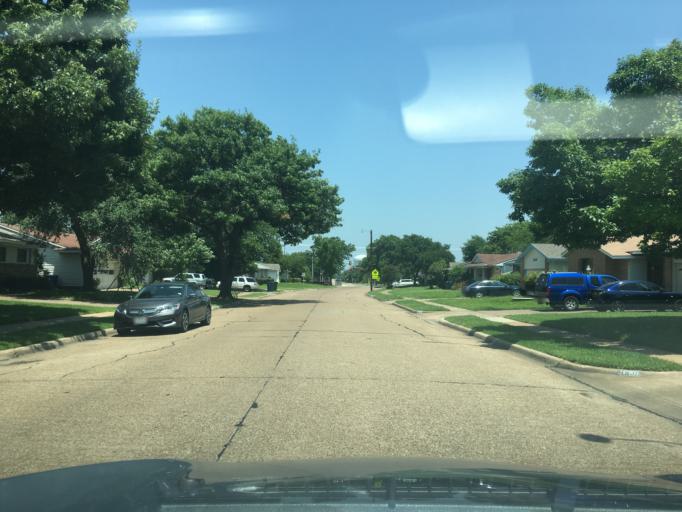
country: US
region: Texas
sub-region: Dallas County
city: Richardson
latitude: 32.9241
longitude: -96.7021
